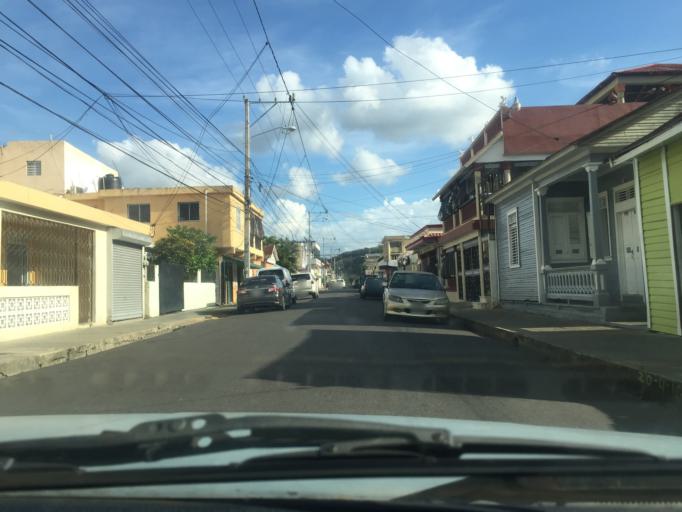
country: DO
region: Santiago
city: Santiago de los Caballeros
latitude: 19.4557
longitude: -70.7124
